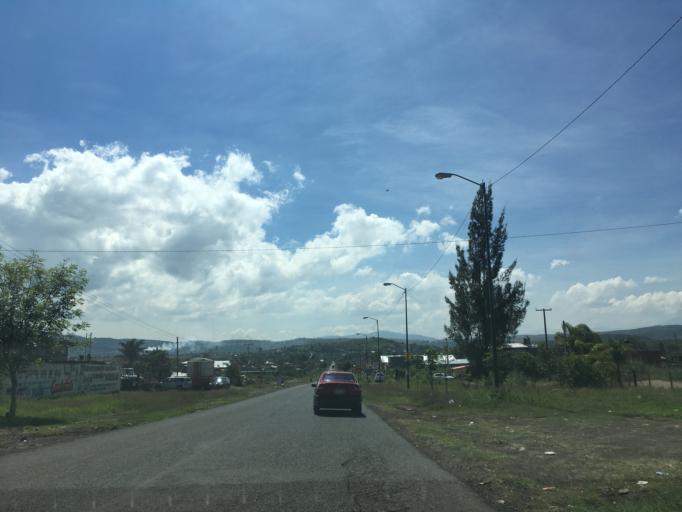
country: MX
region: Michoacan
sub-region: Morelia
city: Villas de la Loma
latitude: 19.6868
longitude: -101.2794
